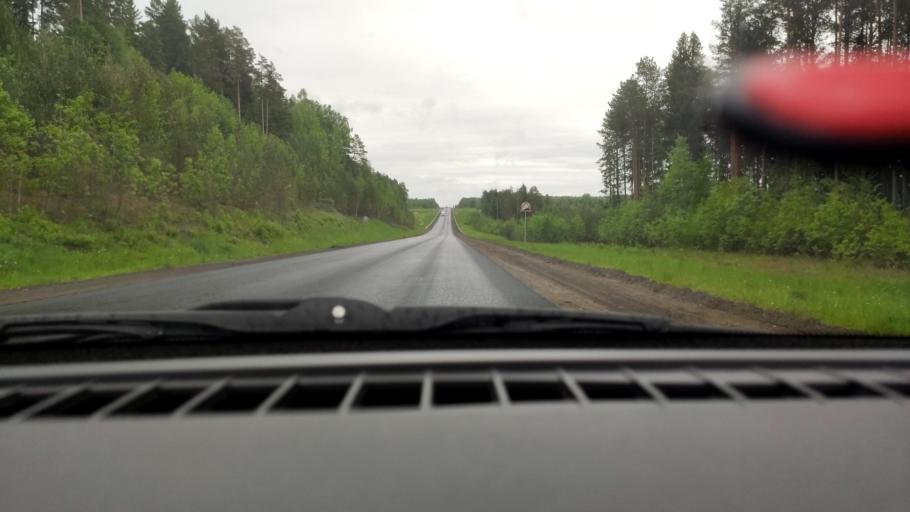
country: RU
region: Perm
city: Karagay
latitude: 58.2527
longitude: 54.9080
